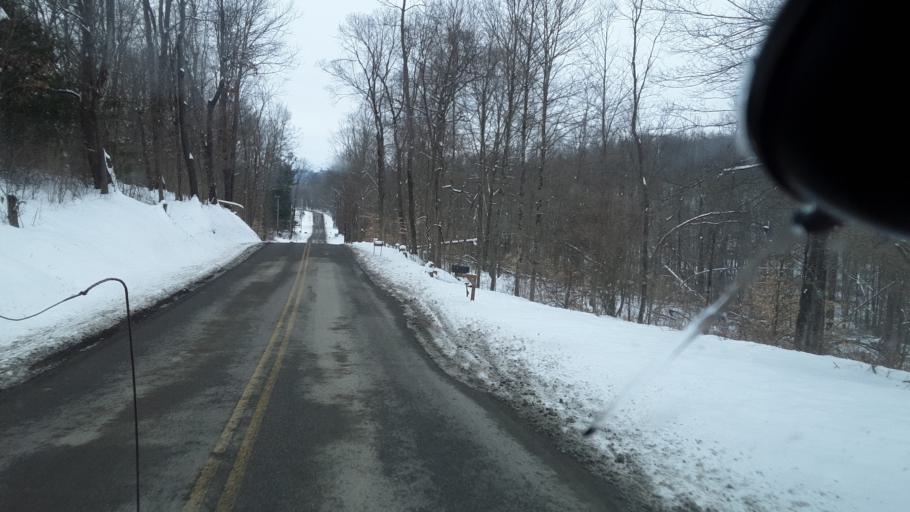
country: US
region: Ohio
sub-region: Perry County
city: Somerset
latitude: 39.9113
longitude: -82.2280
